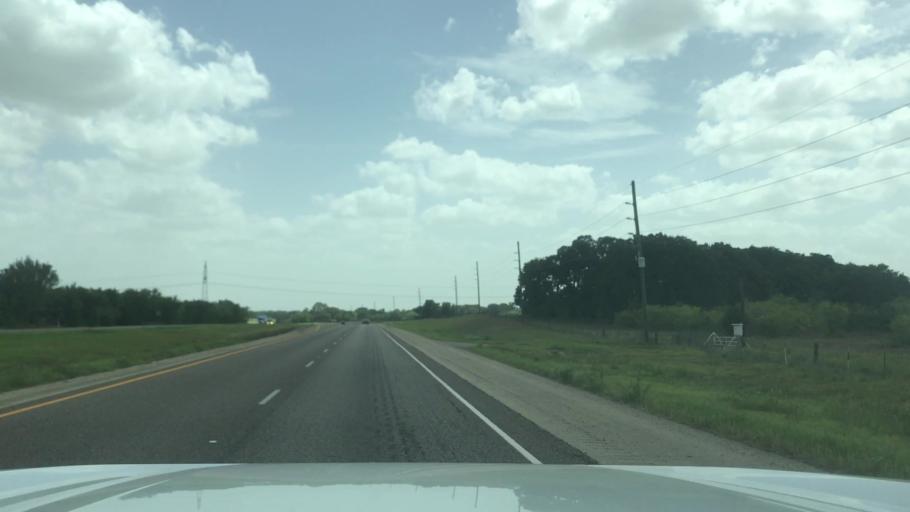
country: US
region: Texas
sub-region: Robertson County
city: Calvert
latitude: 31.1030
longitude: -96.7146
